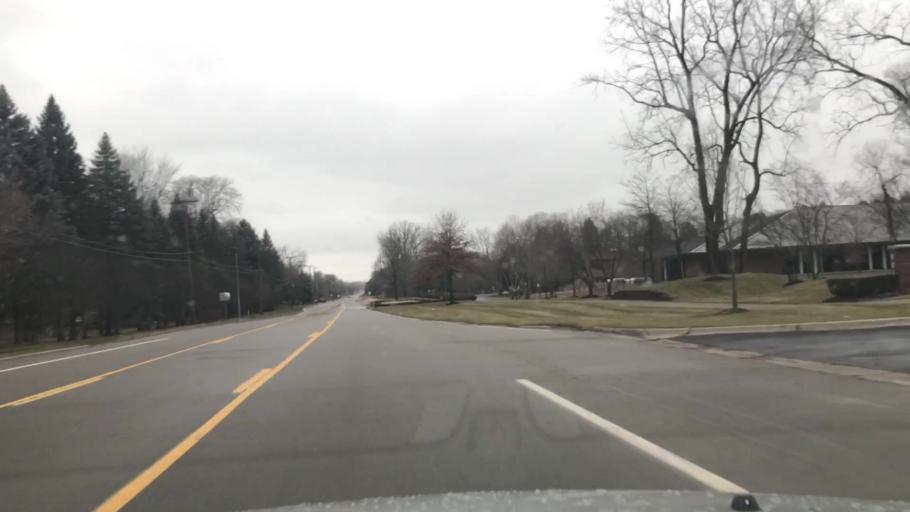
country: US
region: Michigan
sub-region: Oakland County
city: Troy
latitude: 42.6237
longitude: -83.1123
